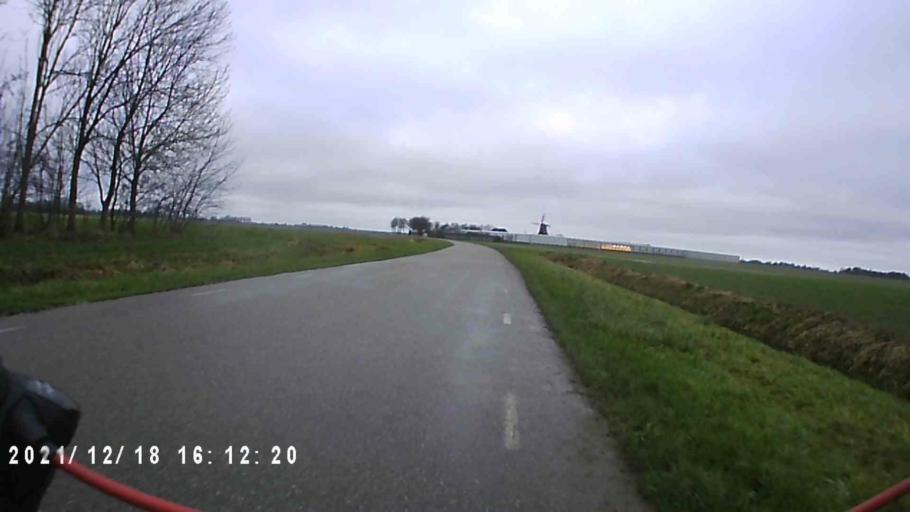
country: NL
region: Friesland
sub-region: Gemeente Dongeradeel
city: Anjum
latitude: 53.3650
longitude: 6.0686
